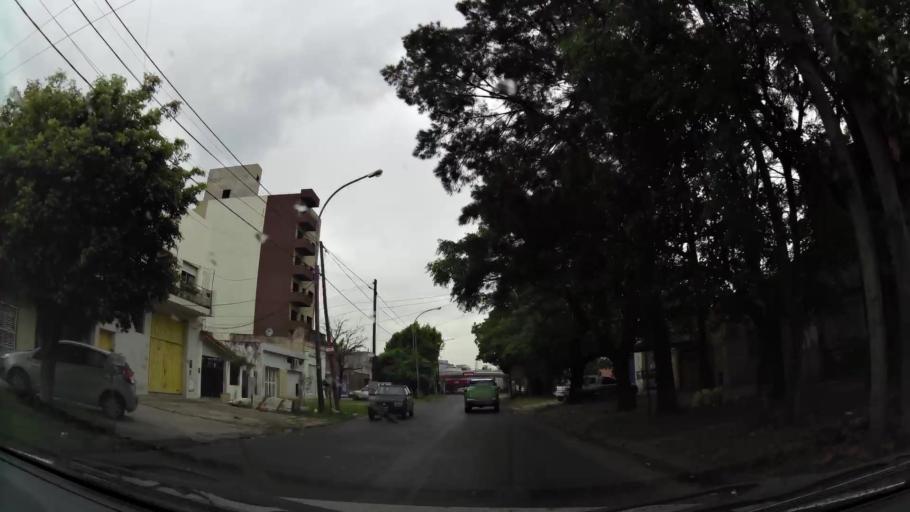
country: AR
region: Buenos Aires
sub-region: Partido de Lanus
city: Lanus
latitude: -34.7011
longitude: -58.4020
